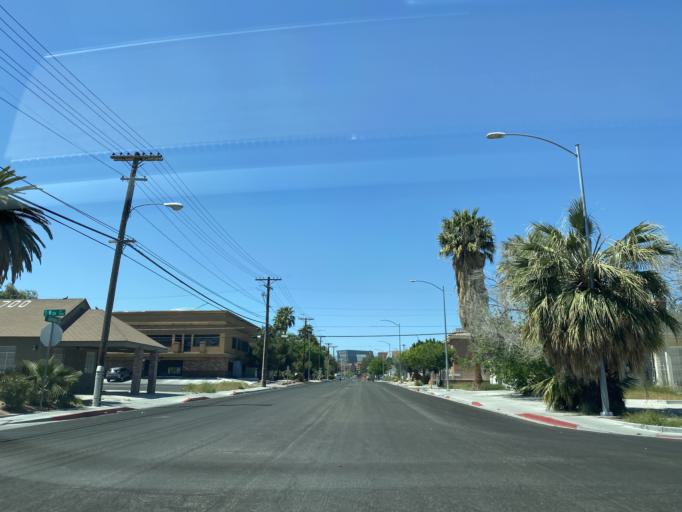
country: US
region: Nevada
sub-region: Clark County
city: Las Vegas
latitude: 36.1603
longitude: -115.1406
